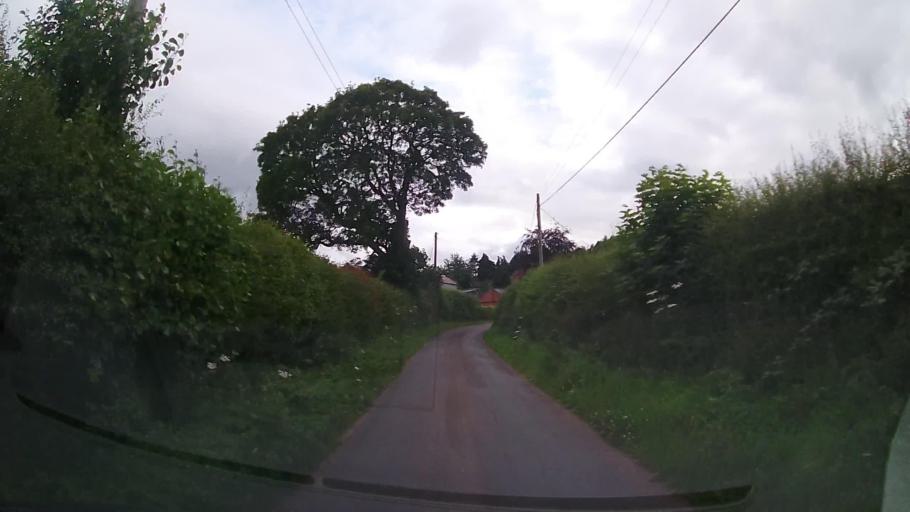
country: GB
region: England
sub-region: Shropshire
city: Prees
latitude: 52.9190
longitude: -2.6930
